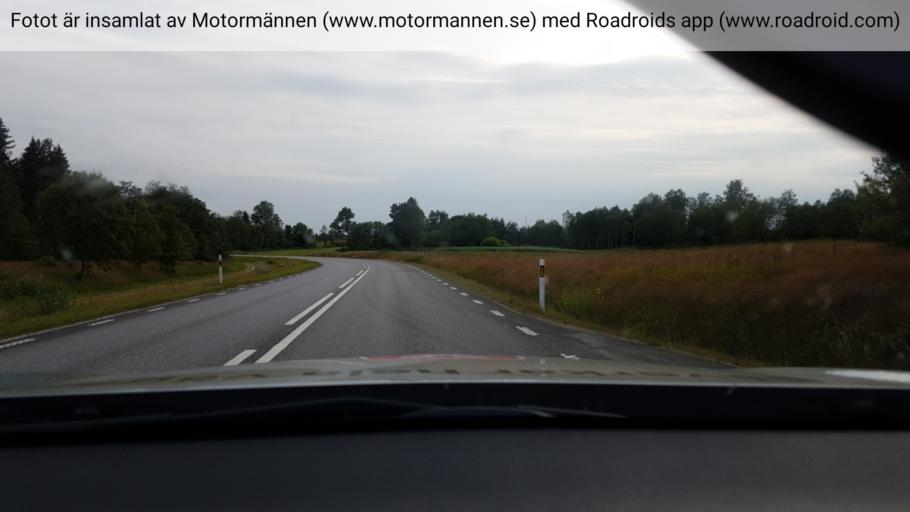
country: SE
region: Vaestra Goetaland
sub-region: Uddevalla Kommun
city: Uddevalla
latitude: 58.4109
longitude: 12.0109
